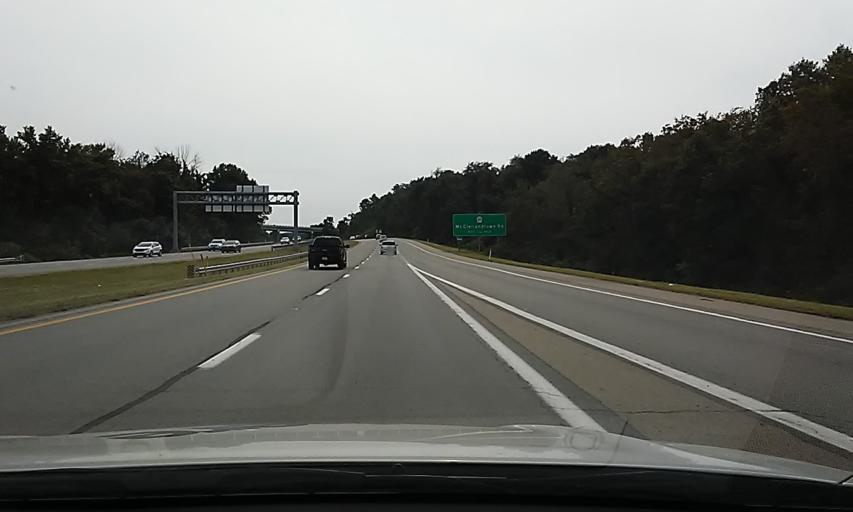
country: US
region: Pennsylvania
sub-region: Fayette County
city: South Uniontown
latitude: 39.9050
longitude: -79.7422
